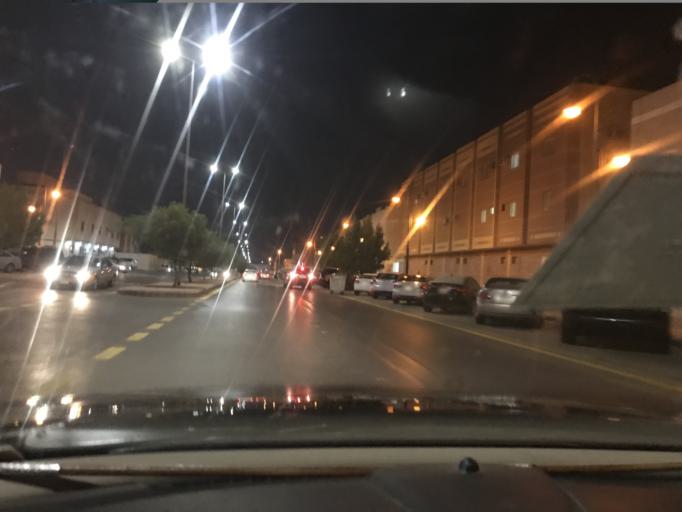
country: SA
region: Ar Riyad
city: Riyadh
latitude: 24.7415
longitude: 46.7697
